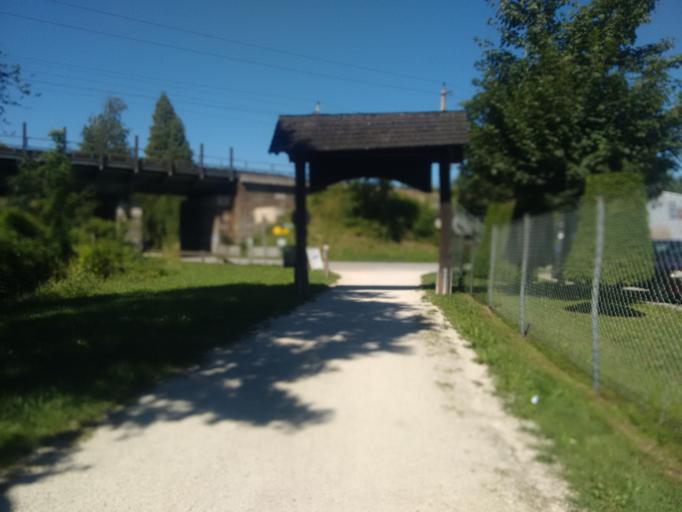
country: AT
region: Upper Austria
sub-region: Politischer Bezirk Grieskirchen
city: Bad Schallerbach
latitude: 48.2248
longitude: 13.9380
